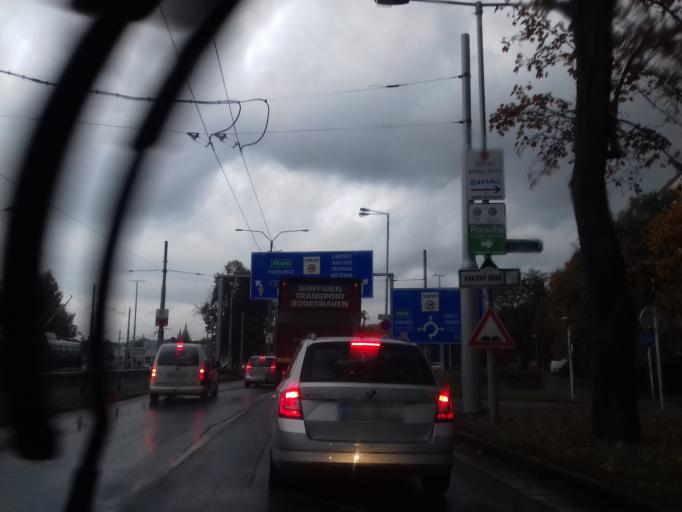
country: CZ
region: Kralovehradecky
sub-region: Okres Hradec Kralove
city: Hradec Kralove
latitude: 50.2012
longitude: 15.8432
